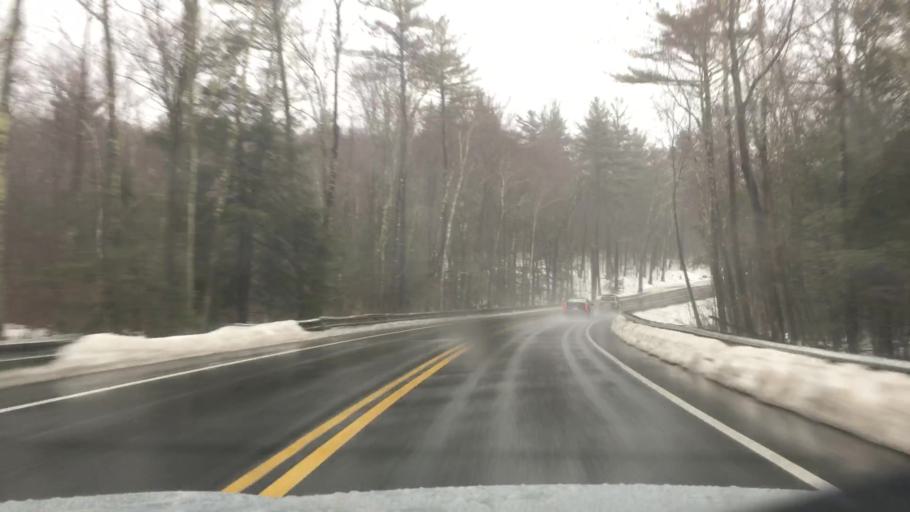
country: US
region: Massachusetts
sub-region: Franklin County
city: Shutesbury
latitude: 42.4754
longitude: -72.3505
